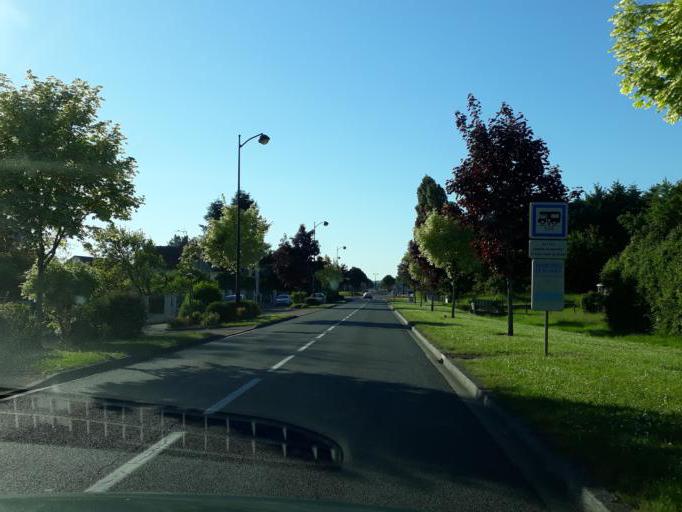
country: FR
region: Centre
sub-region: Departement du Loiret
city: Briare
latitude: 47.6296
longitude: 2.7496
